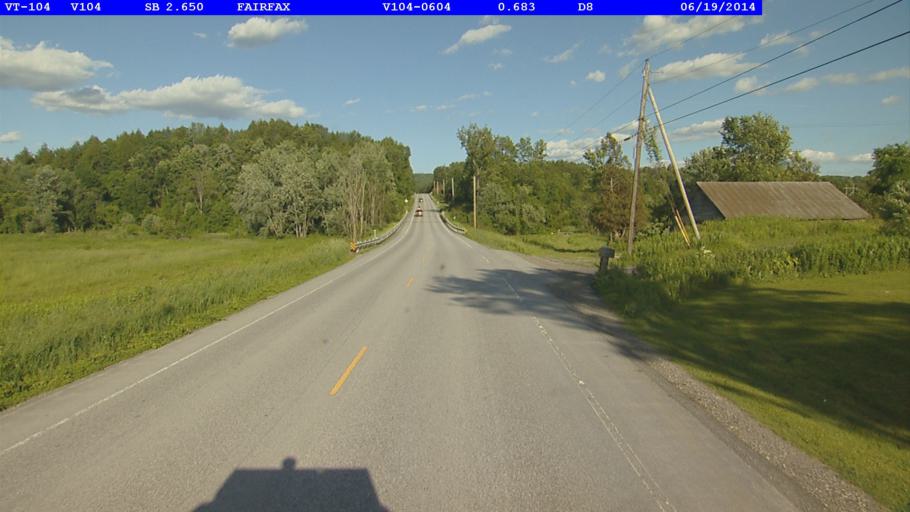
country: US
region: Vermont
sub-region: Chittenden County
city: Jericho
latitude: 44.6409
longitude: -72.9387
